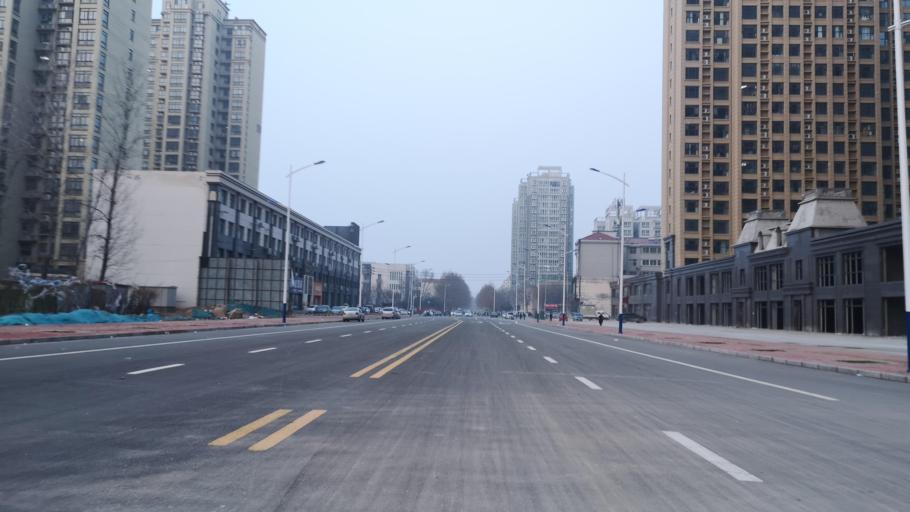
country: CN
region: Henan Sheng
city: Zhongyuanlu
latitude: 35.7514
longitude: 115.0602
